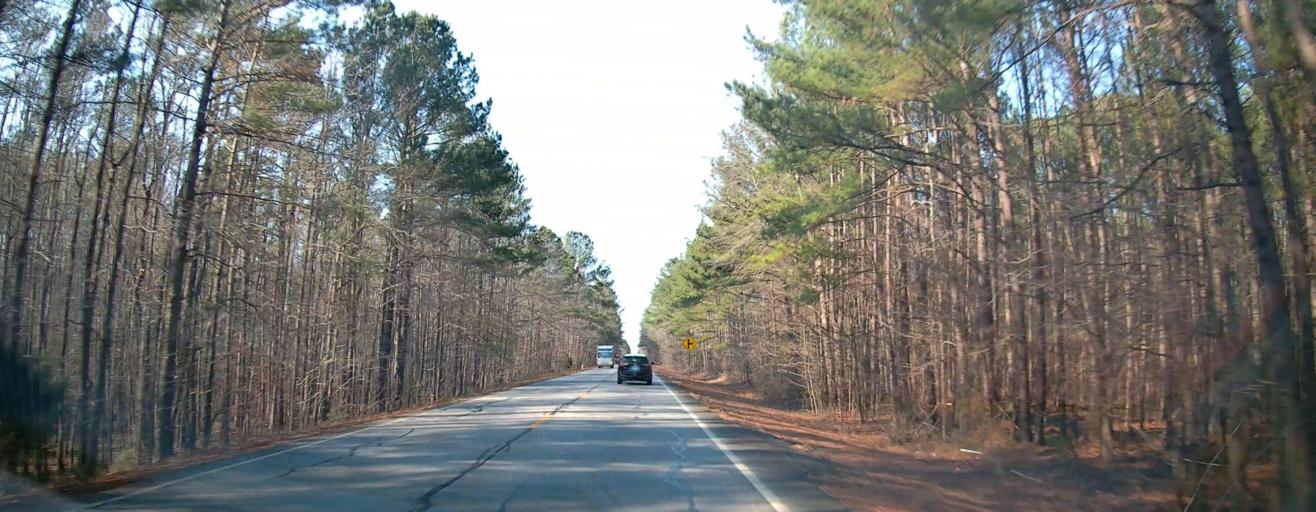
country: US
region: Georgia
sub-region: Butts County
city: Indian Springs
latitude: 33.2019
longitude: -83.8549
